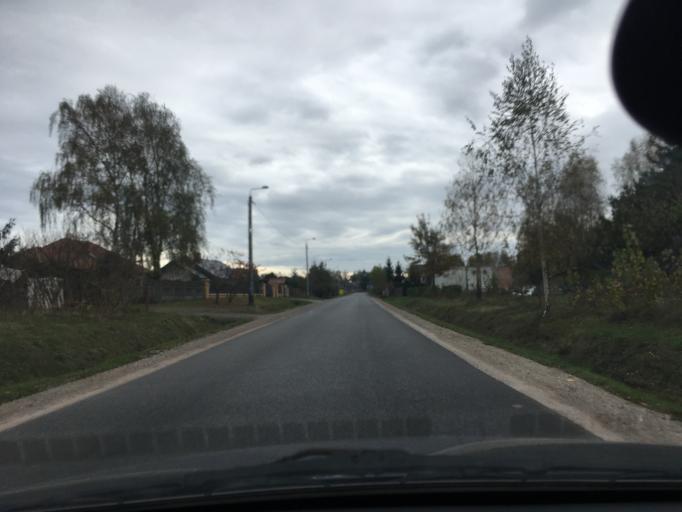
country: PL
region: Lodz Voivodeship
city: Zabia Wola
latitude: 52.0121
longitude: 20.6913
